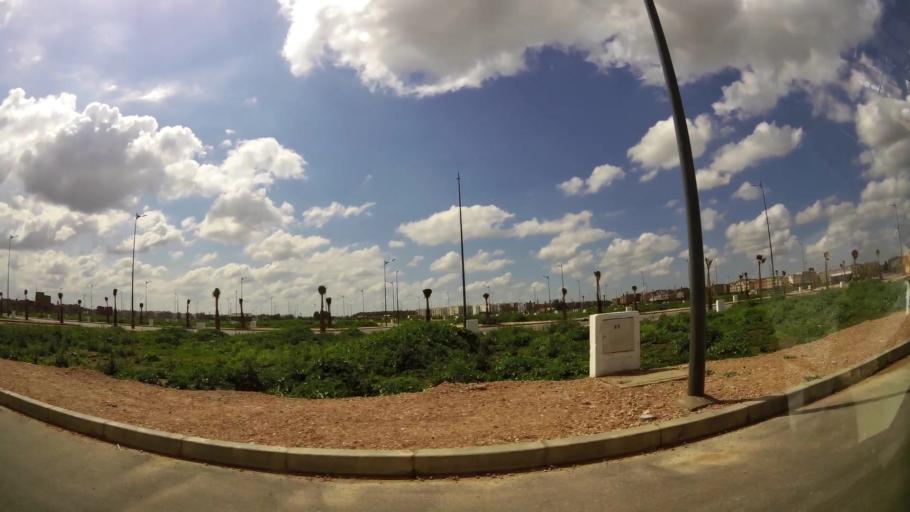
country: MA
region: Grand Casablanca
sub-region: Mediouna
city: Mediouna
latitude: 33.3666
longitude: -7.5322
